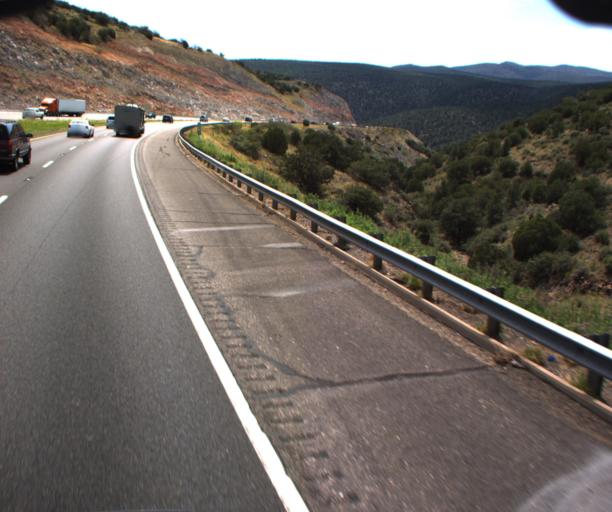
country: US
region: Arizona
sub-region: Yavapai County
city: Camp Verde
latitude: 34.5335
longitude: -111.9596
